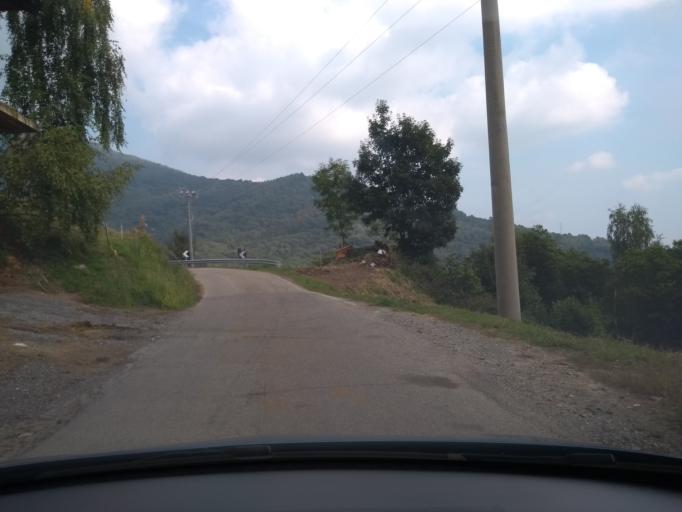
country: IT
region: Piedmont
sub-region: Provincia di Torino
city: Corio
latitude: 45.3277
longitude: 7.5174
